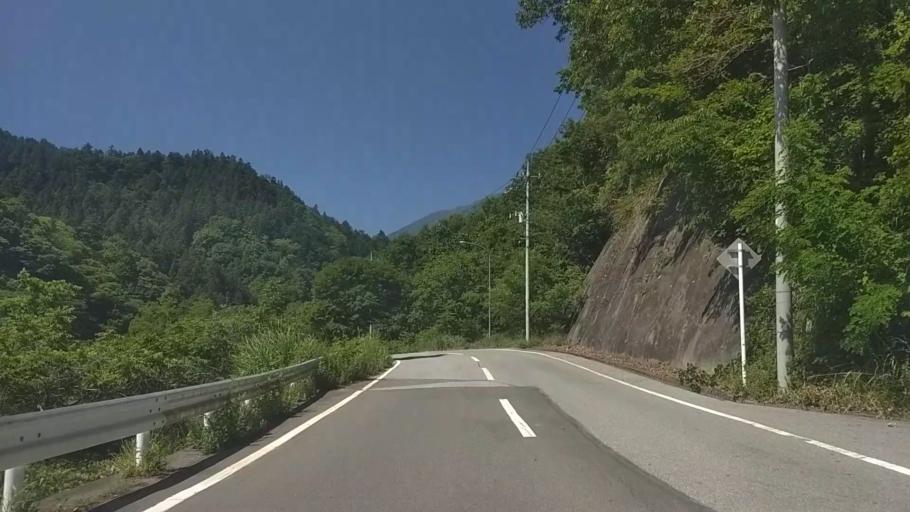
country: JP
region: Yamanashi
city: Ryuo
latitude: 35.5095
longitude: 138.4386
